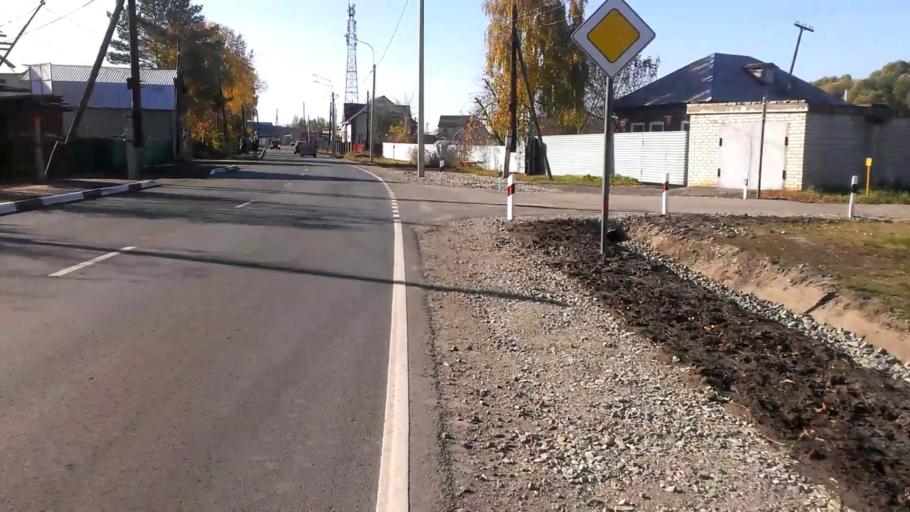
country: RU
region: Altai Krai
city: Sannikovo
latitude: 53.3176
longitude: 83.9489
